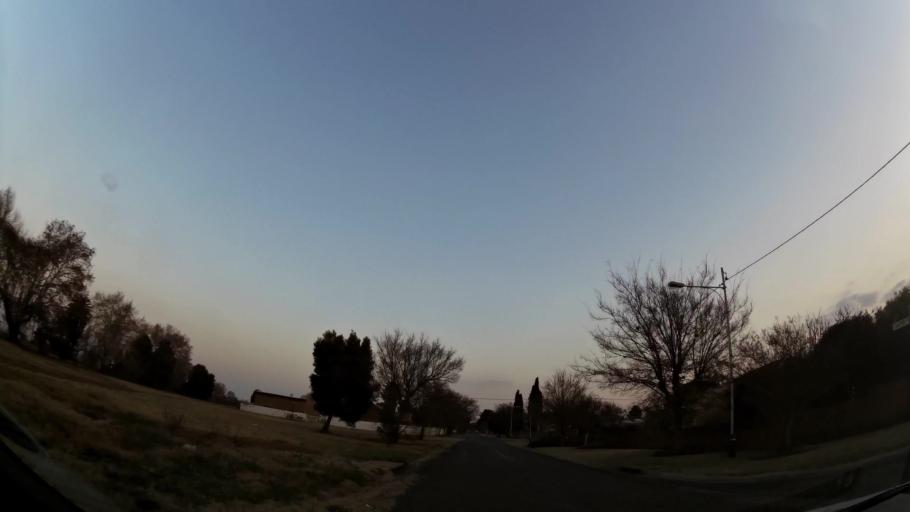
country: ZA
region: Gauteng
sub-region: Ekurhuleni Metropolitan Municipality
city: Nigel
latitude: -26.3485
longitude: 28.4408
